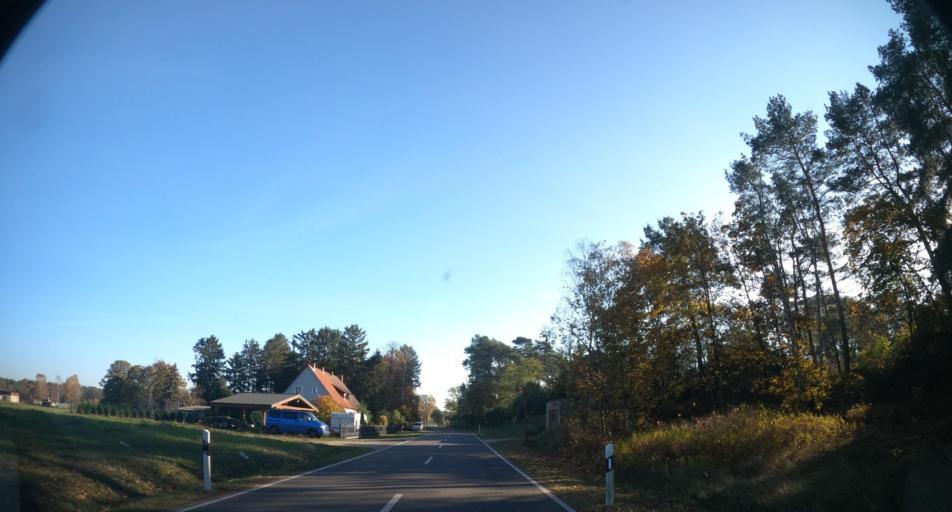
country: DE
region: Mecklenburg-Vorpommern
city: Ahlbeck
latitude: 53.6272
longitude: 14.2682
